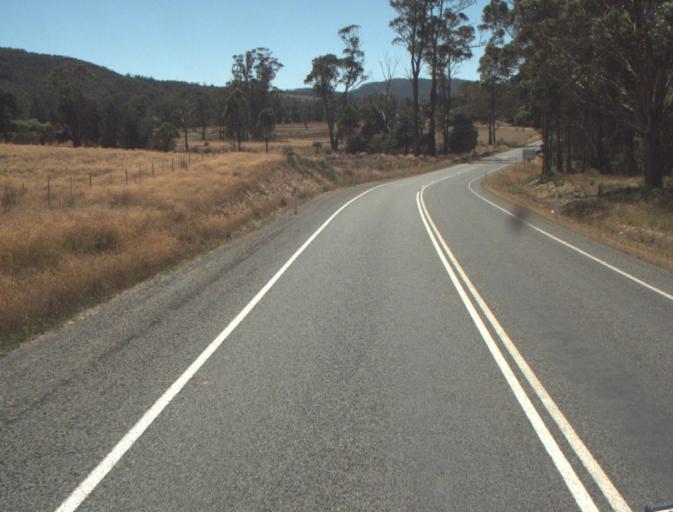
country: AU
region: Tasmania
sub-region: Launceston
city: Newstead
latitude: -41.3326
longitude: 147.3498
